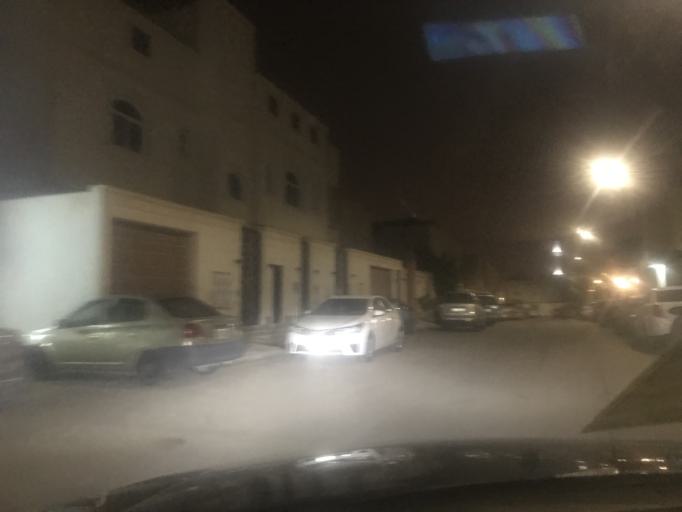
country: SA
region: Ar Riyad
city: Riyadh
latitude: 24.6924
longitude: 46.5981
